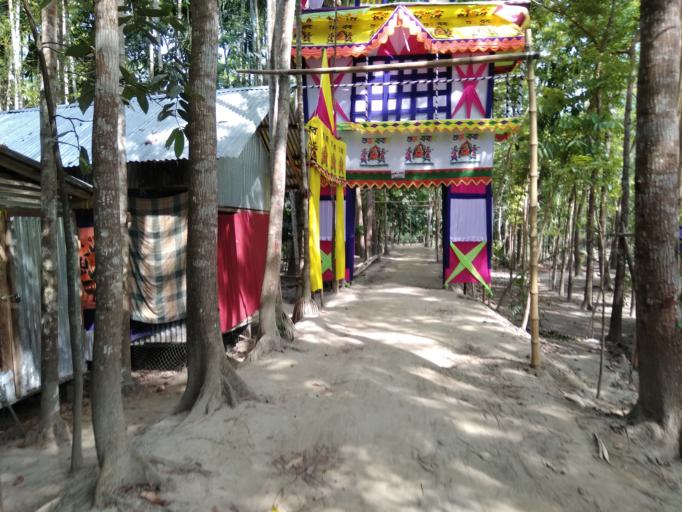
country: BD
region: Barisal
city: Gaurnadi
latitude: 22.9923
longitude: 90.3714
